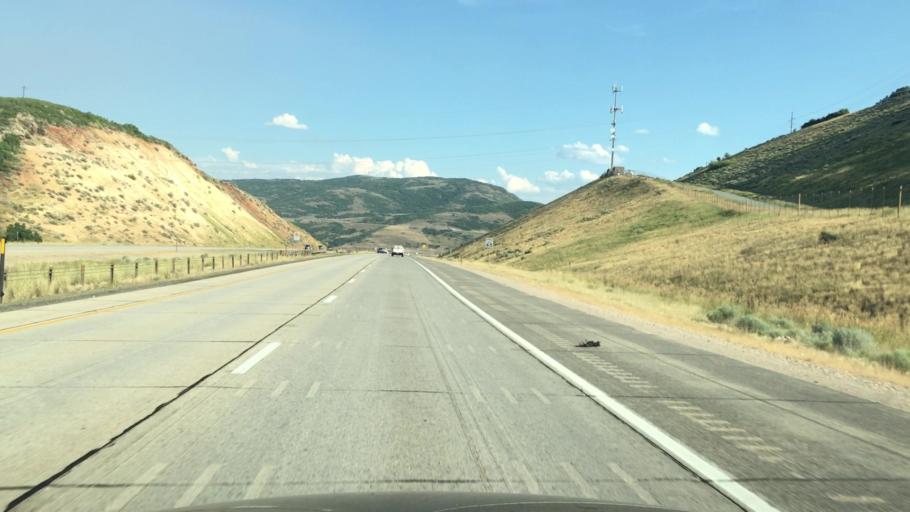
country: US
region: Utah
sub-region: Summit County
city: Park City
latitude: 40.6170
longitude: -111.4352
